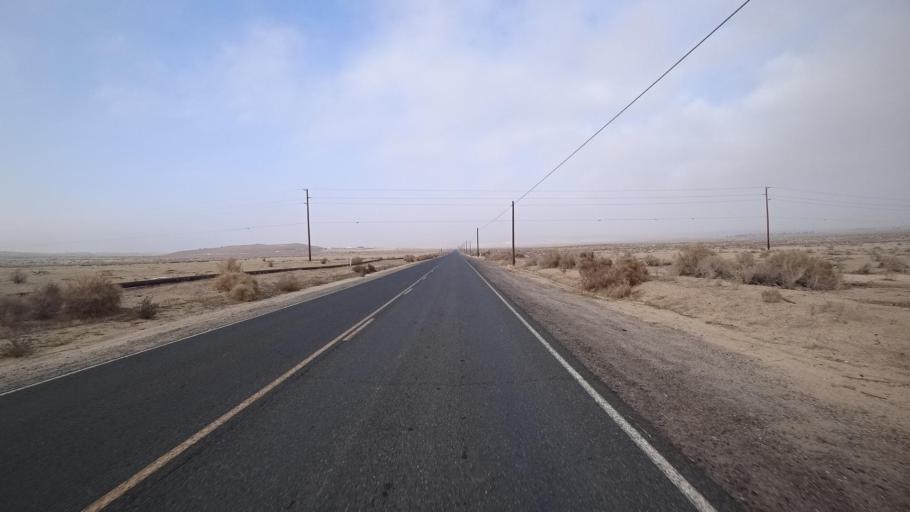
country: US
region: California
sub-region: Kern County
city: Ford City
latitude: 35.1938
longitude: -119.4456
